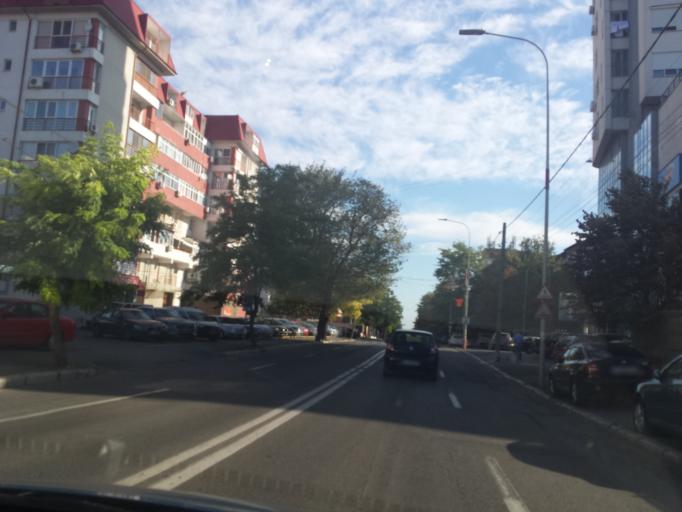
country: RO
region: Tulcea
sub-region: Municipiul Tulcea
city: Tulcea
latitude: 45.1660
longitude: 28.7934
